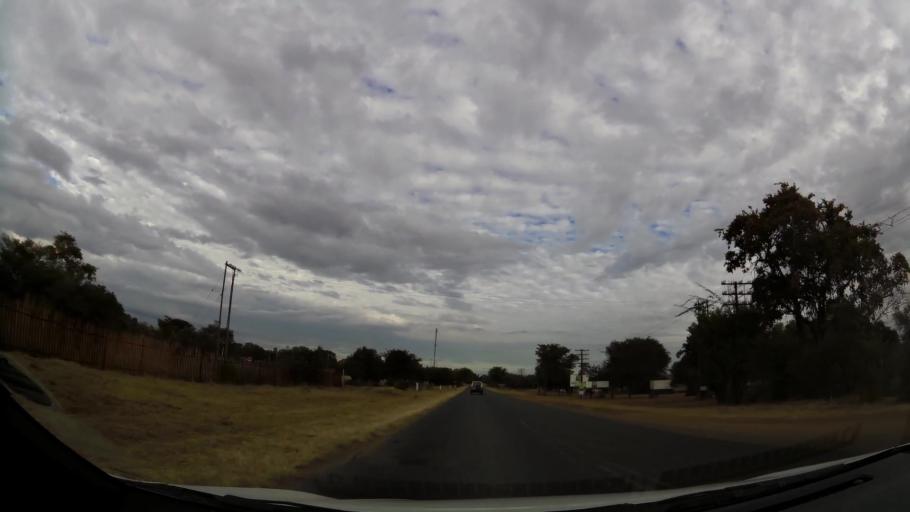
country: ZA
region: Limpopo
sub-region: Waterberg District Municipality
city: Modimolle
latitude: -24.5094
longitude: 28.7051
